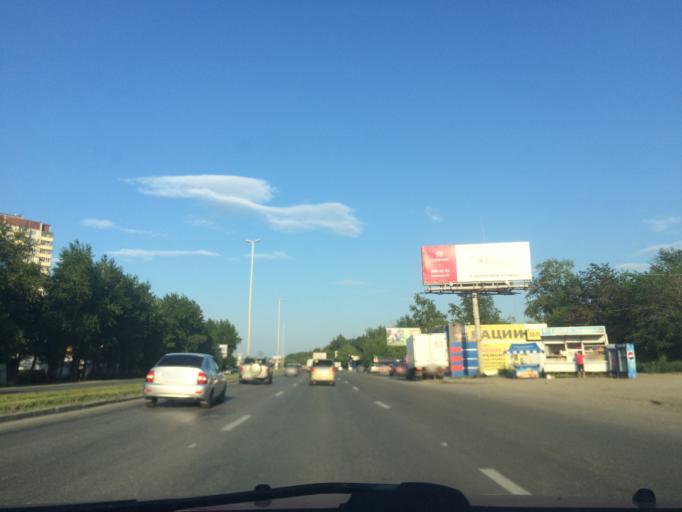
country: RU
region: Sverdlovsk
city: Yekaterinburg
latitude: 56.8244
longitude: 60.6935
